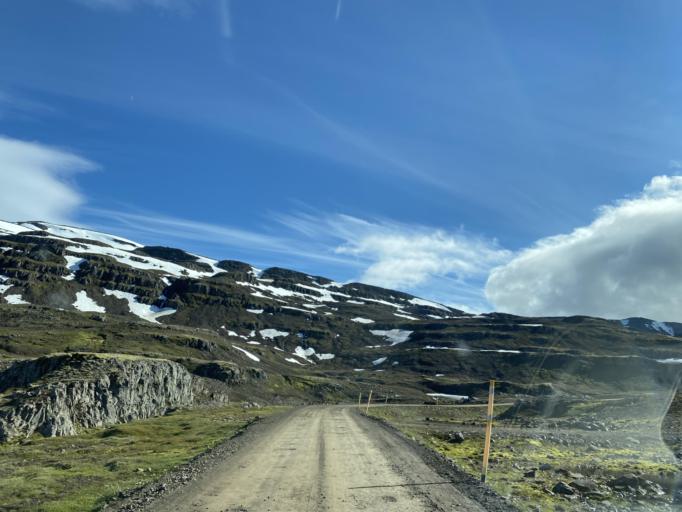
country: IS
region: East
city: Eskifjoerdur
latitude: 65.1709
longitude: -14.1206
